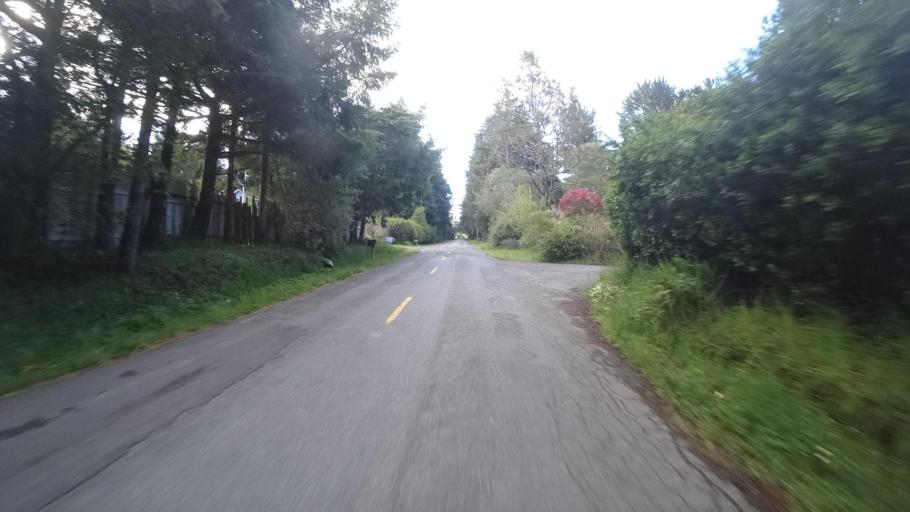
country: US
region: California
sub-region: Humboldt County
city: Westhaven-Moonstone
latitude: 41.0581
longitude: -124.1256
